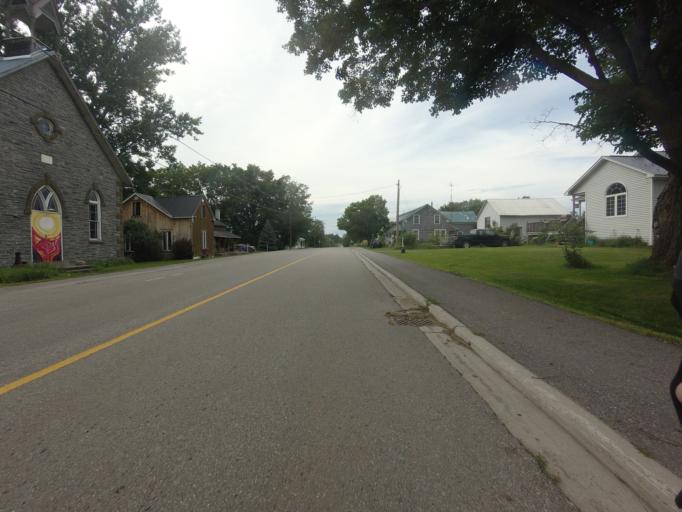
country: CA
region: Ontario
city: Perth
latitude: 45.0966
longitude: -76.3947
